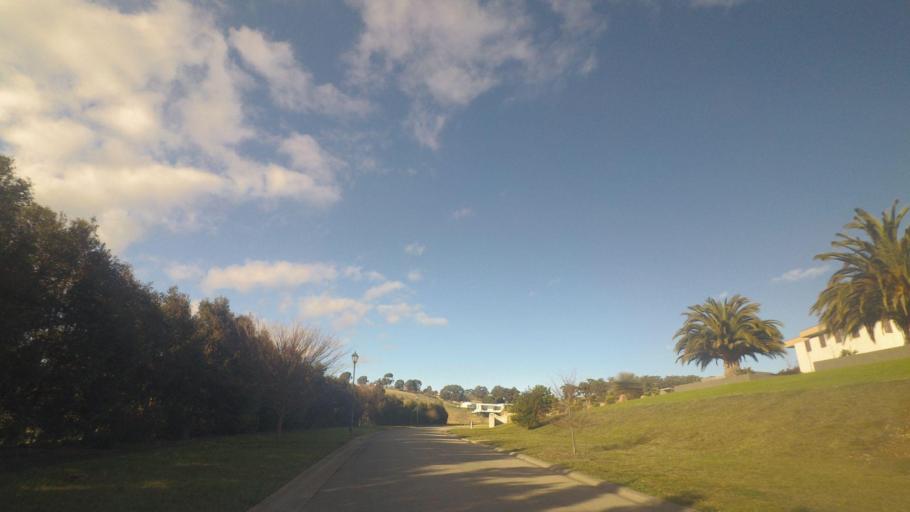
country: AU
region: Victoria
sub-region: Yarra Ranges
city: Lysterfield
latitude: -37.9172
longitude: 145.2915
